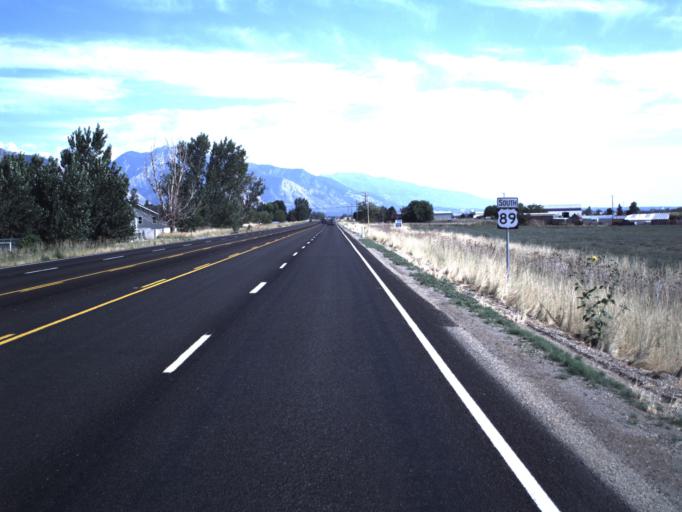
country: US
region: Utah
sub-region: Box Elder County
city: South Willard
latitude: 41.3311
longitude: -112.0243
